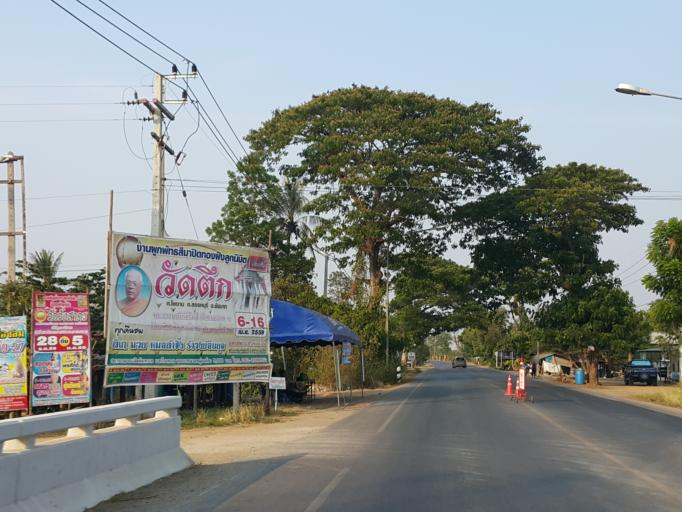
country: TH
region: Chai Nat
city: Sankhaburi
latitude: 15.0682
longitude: 100.1685
